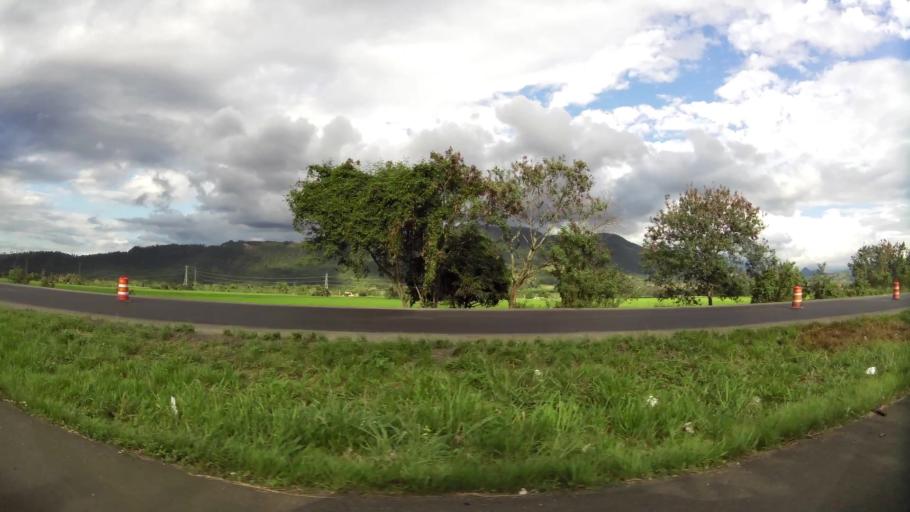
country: DO
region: Monsenor Nouel
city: Bonao
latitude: 18.8976
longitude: -70.3695
